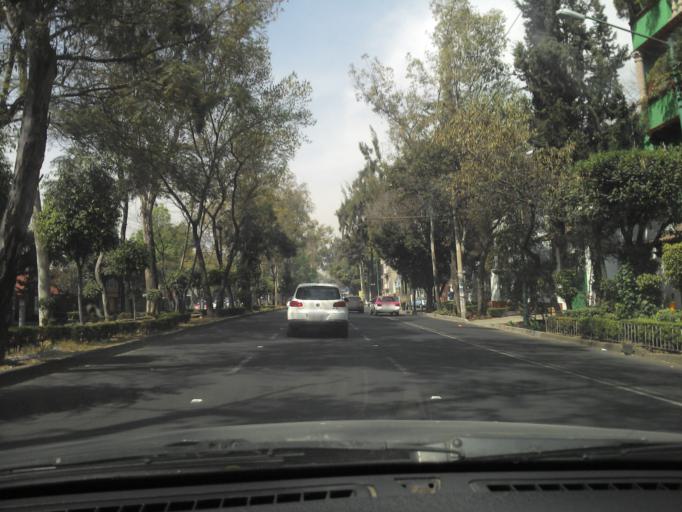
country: MX
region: Mexico City
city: Coyoacan
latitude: 19.3431
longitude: -99.1515
